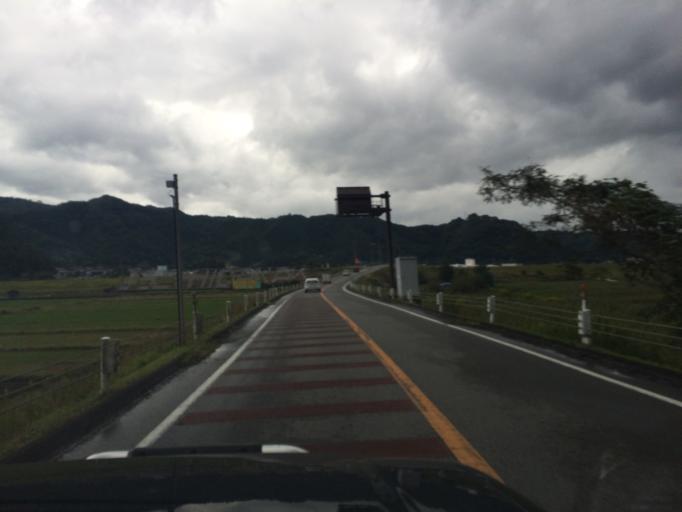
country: JP
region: Hyogo
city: Toyooka
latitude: 35.4515
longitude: 134.7805
